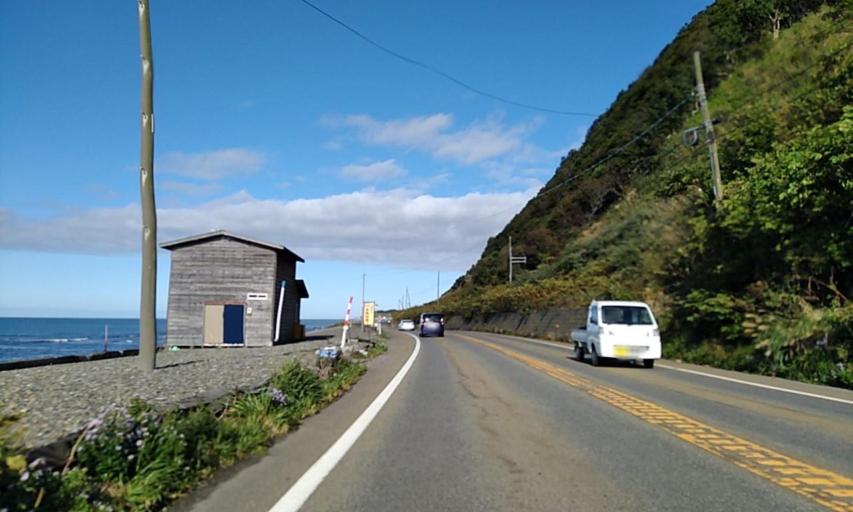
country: JP
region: Hokkaido
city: Shizunai-furukawacho
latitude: 42.2593
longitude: 142.5259
